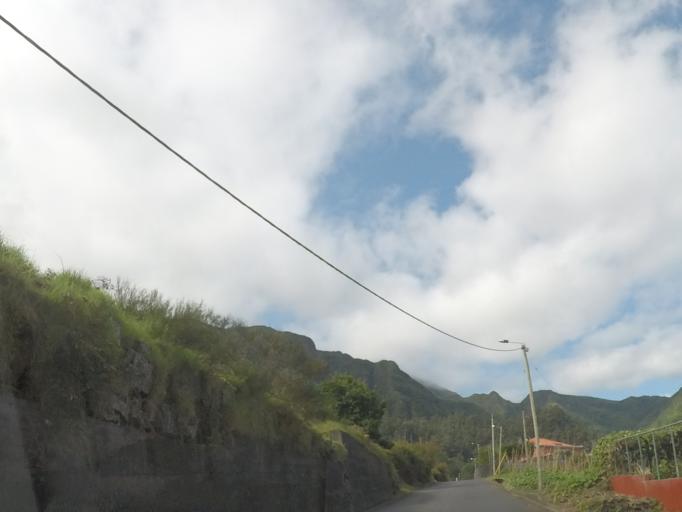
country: PT
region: Madeira
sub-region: Sao Vicente
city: Sao Vicente
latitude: 32.7799
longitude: -17.0429
